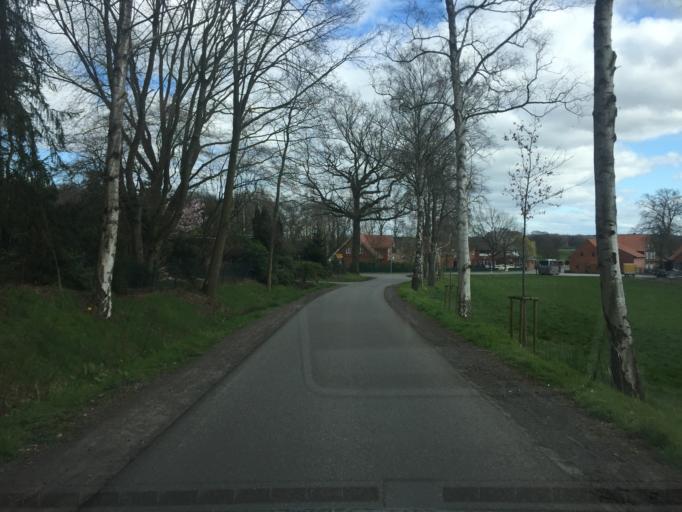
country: DE
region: Lower Saxony
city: Bruchhausen-Vilsen
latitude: 52.8075
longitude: 9.0008
